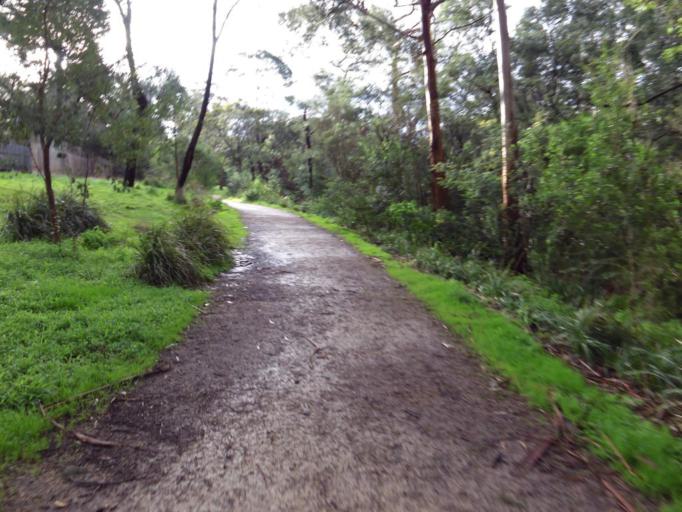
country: AU
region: Victoria
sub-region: Monash
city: Notting Hill
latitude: -37.8829
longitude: 145.1354
